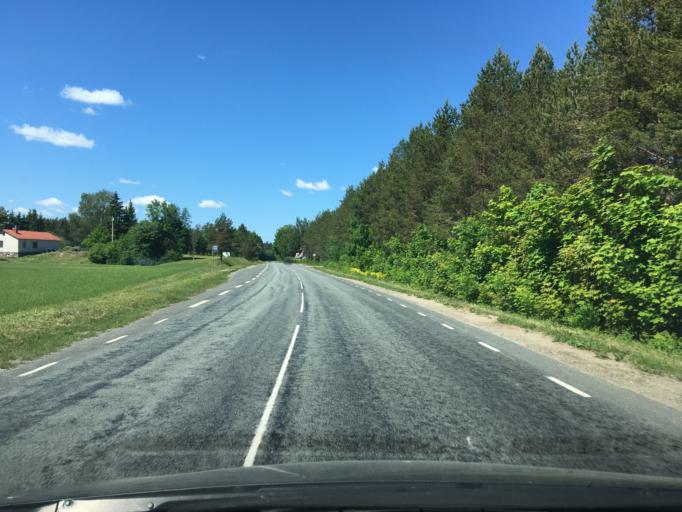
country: EE
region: Harju
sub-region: Rae vald
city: Vaida
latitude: 59.2033
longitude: 24.9536
